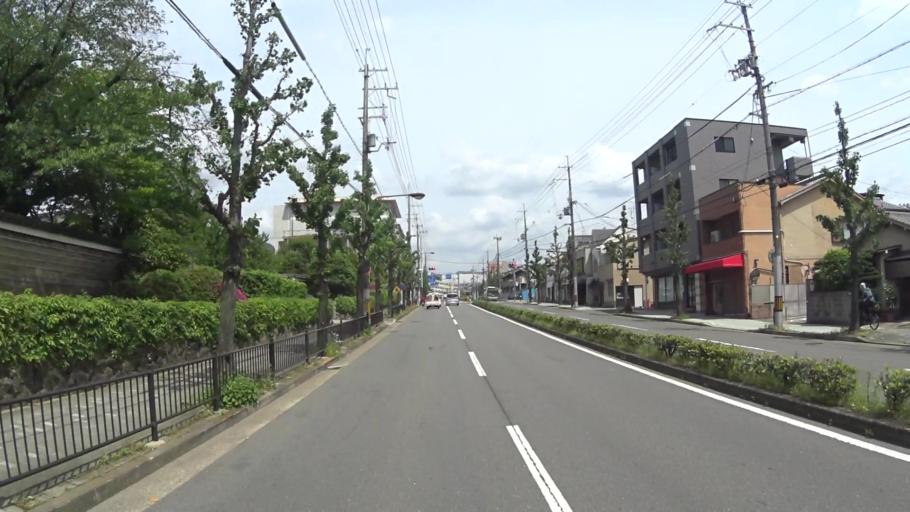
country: JP
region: Kyoto
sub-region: Kyoto-shi
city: Kamigyo-ku
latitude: 35.0386
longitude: 135.7393
